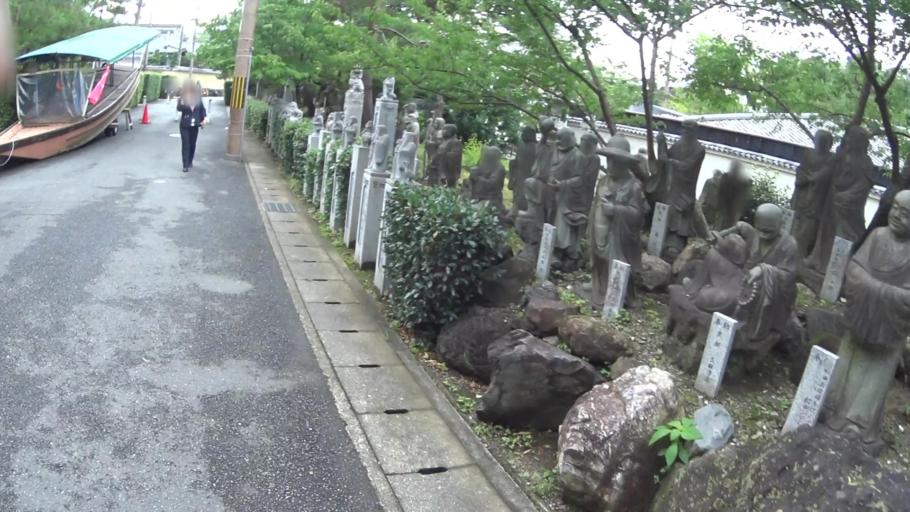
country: JP
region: Kyoto
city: Muko
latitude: 35.0145
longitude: 135.6743
